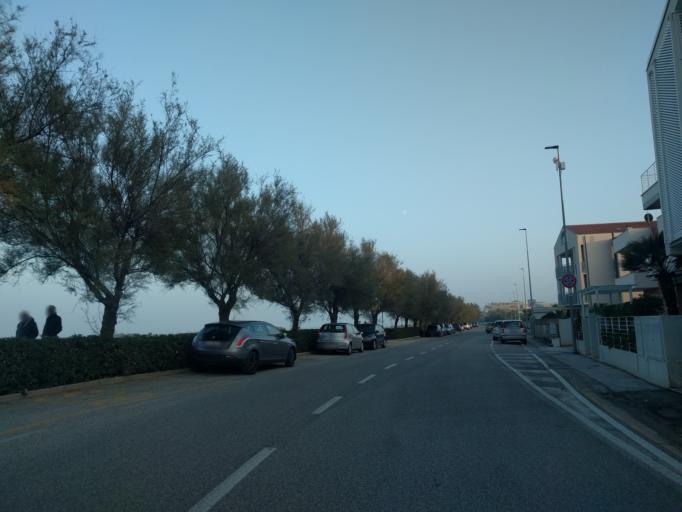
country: IT
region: The Marches
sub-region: Provincia di Ancona
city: Senigallia
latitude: 43.7420
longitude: 13.1843
